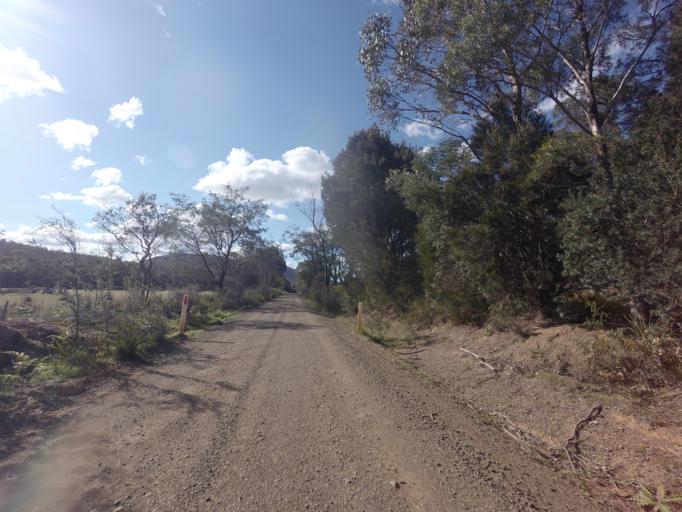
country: AU
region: Tasmania
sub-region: Break O'Day
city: St Helens
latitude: -41.8662
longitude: 148.0216
